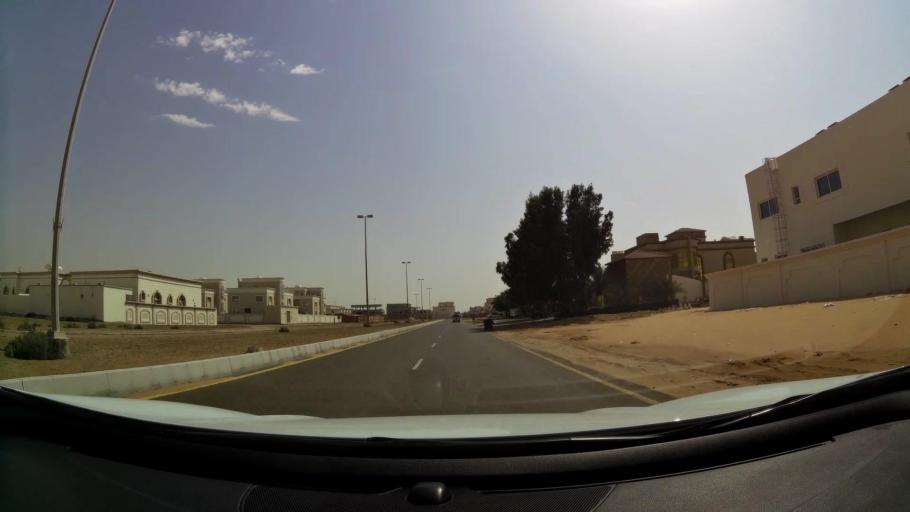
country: AE
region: Abu Dhabi
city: Abu Dhabi
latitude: 24.3349
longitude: 54.5487
